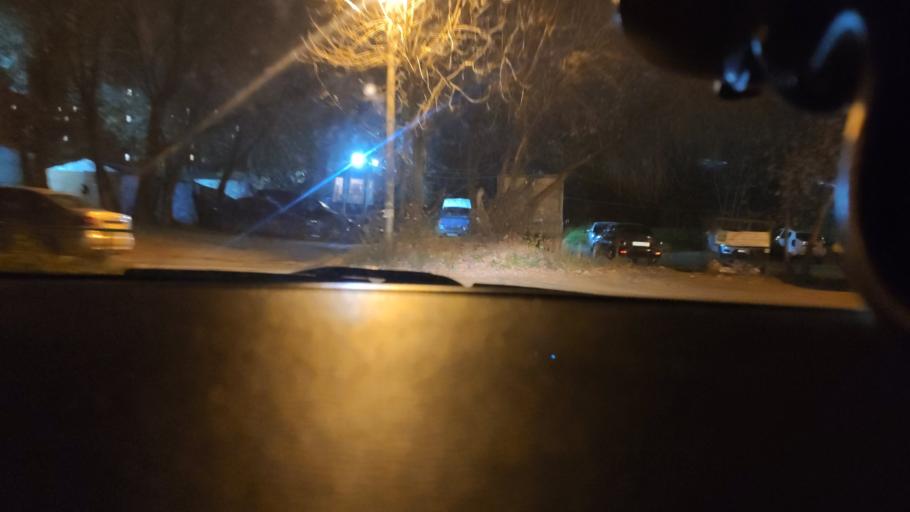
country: RU
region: Perm
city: Kondratovo
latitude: 57.9654
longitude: 56.1826
